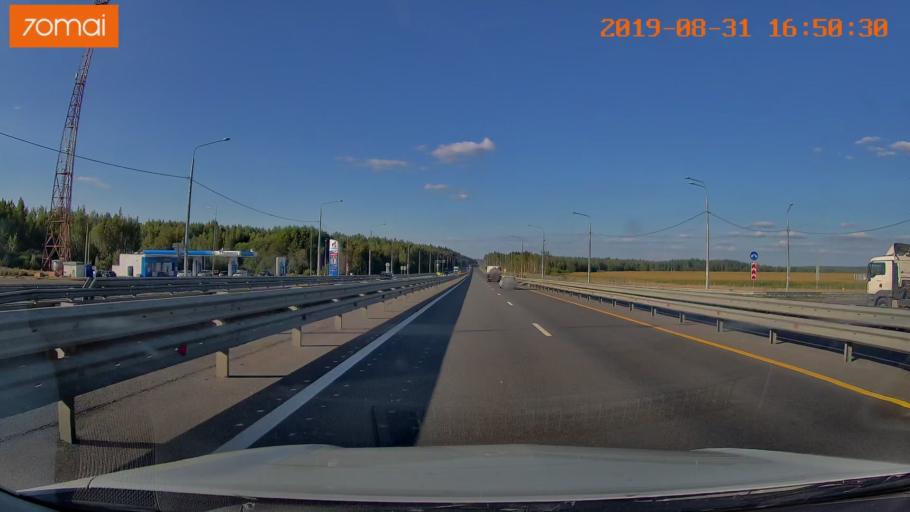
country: RU
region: Kaluga
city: Pyatovskiy
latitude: 54.7098
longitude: 36.1631
